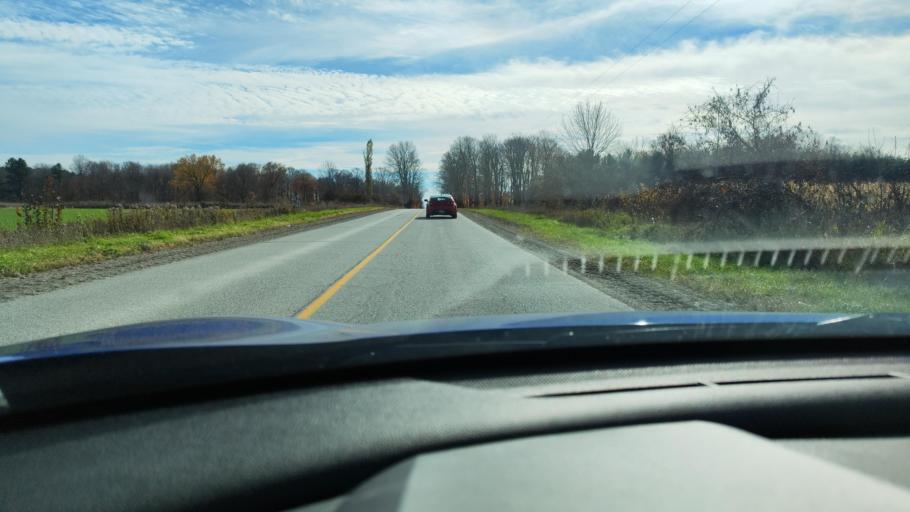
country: CA
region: Ontario
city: Wasaga Beach
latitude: 44.4582
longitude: -80.0029
